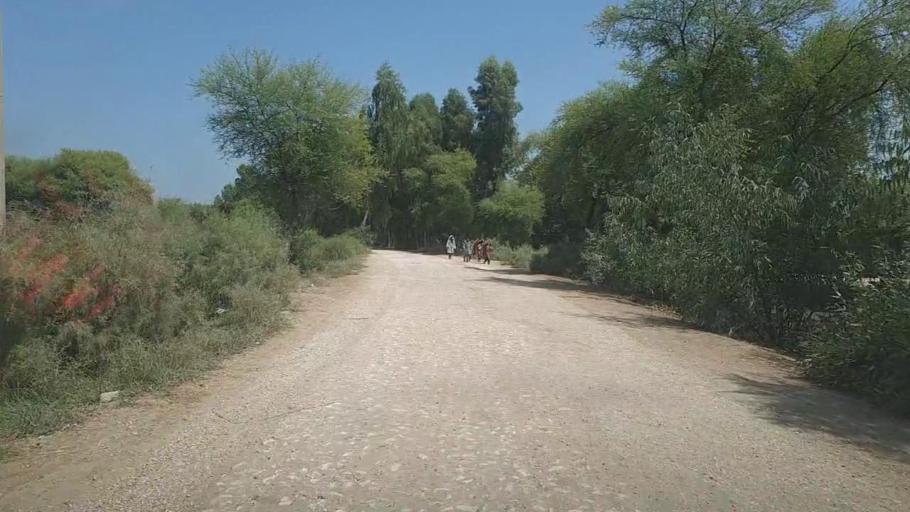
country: PK
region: Sindh
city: Kandhkot
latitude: 28.2710
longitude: 69.2283
